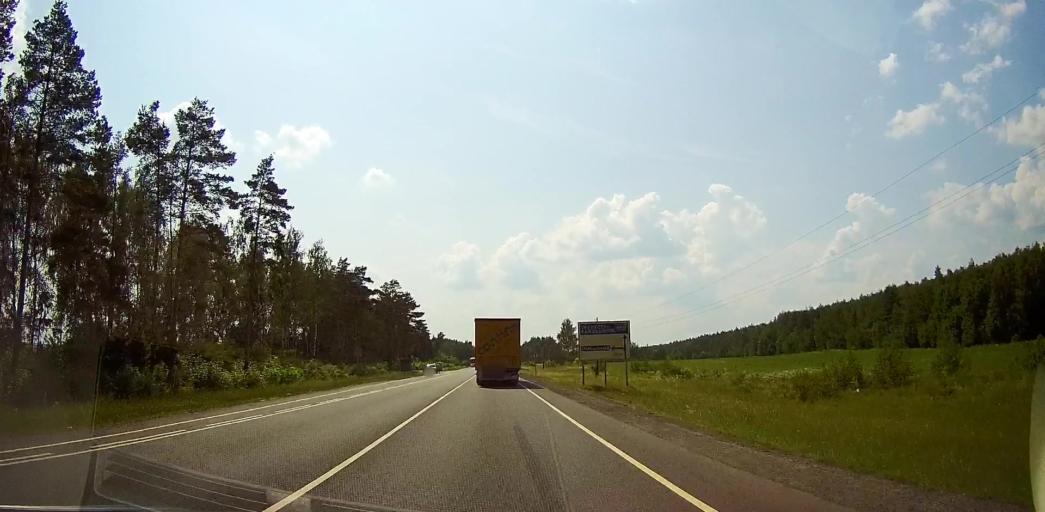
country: RU
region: Moskovskaya
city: Meshcherino
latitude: 55.1754
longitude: 38.3350
